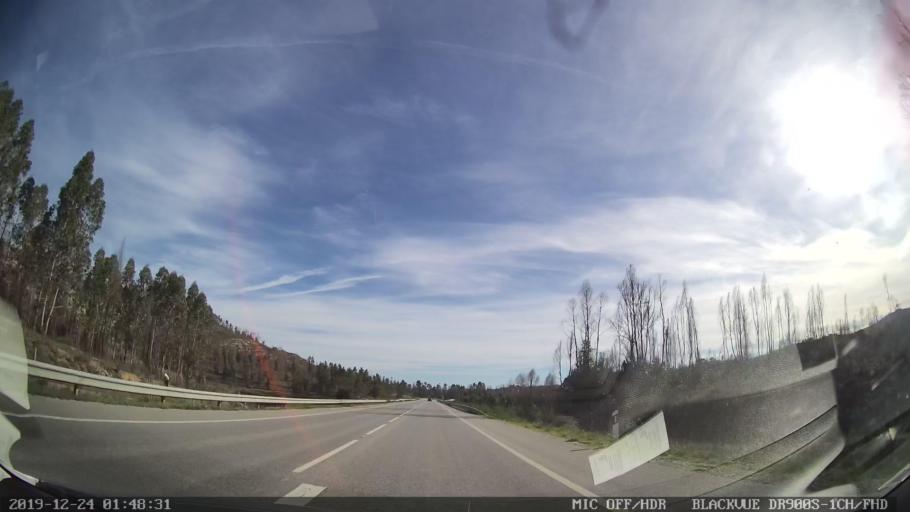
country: PT
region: Portalegre
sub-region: Nisa
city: Nisa
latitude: 39.5207
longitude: -7.7752
